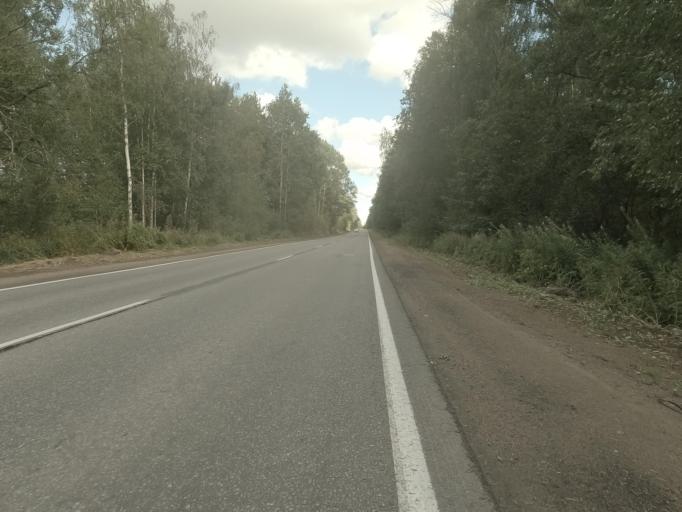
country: RU
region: Leningrad
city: Romanovka
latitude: 60.0212
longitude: 30.7255
